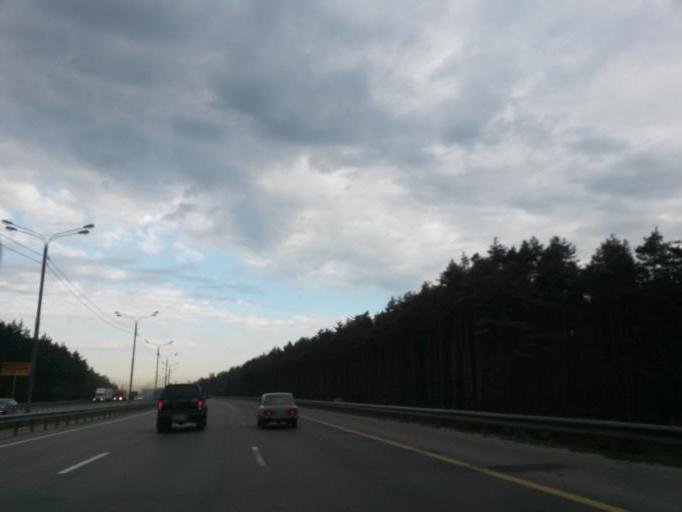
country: RU
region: Moskovskaya
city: Domodedovo
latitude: 55.4497
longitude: 37.7913
